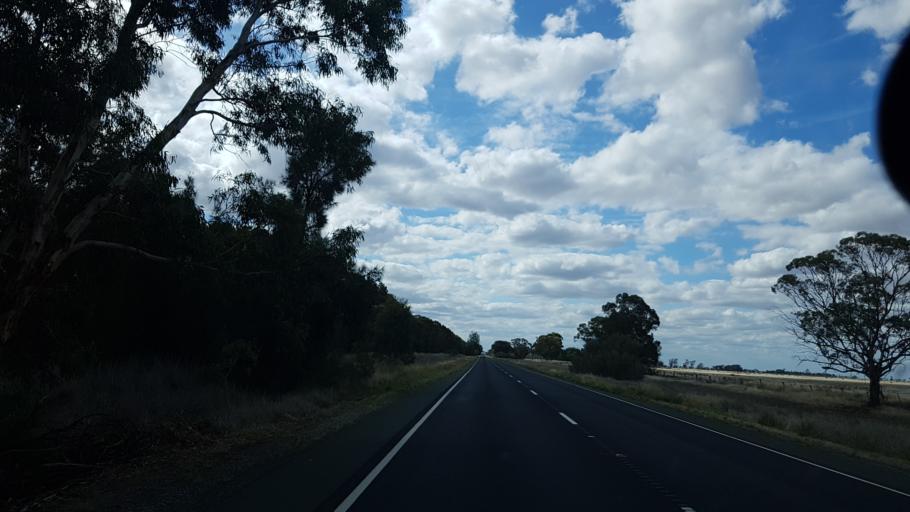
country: AU
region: Victoria
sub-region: Swan Hill
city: Swan Hill
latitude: -35.9856
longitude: 143.9456
